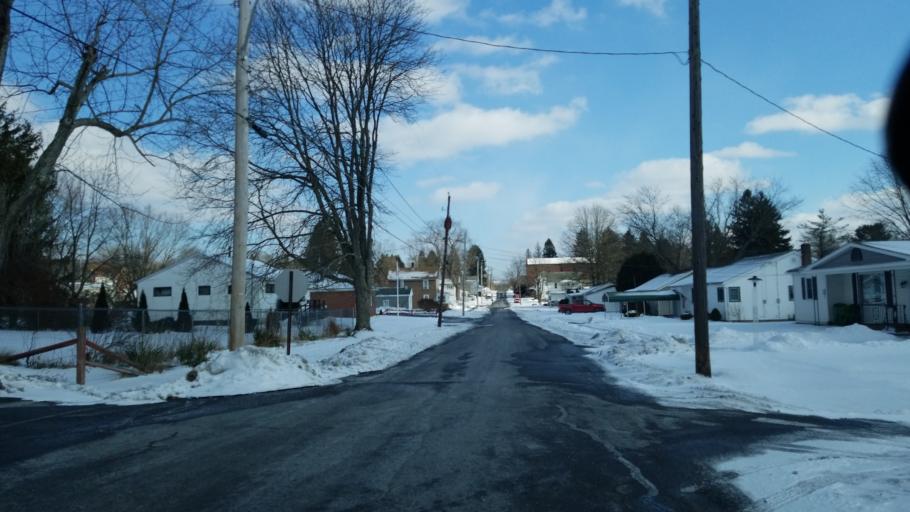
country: US
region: Pennsylvania
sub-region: Jefferson County
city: Falls Creek
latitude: 41.1432
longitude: -78.8022
